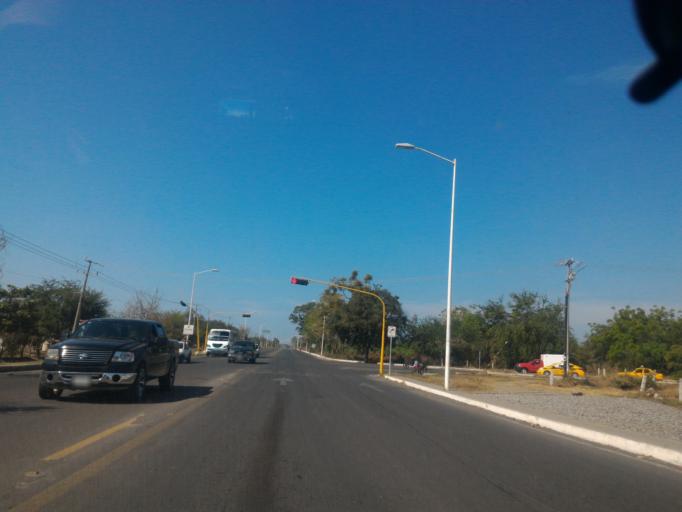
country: MX
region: Colima
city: Tecoman
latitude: 18.9082
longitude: -103.8893
